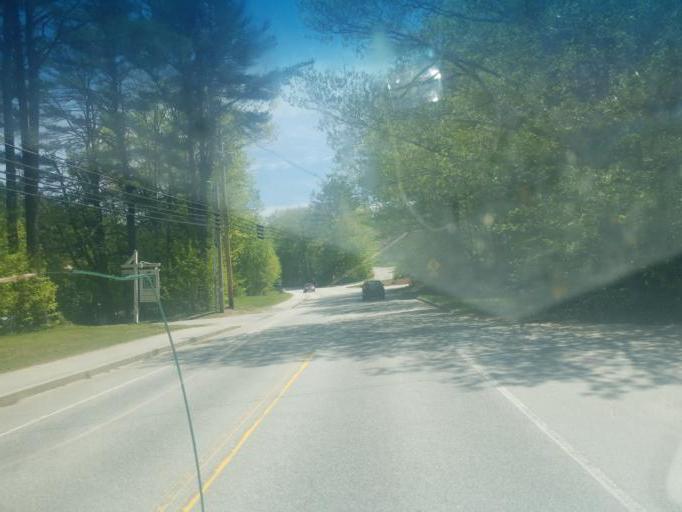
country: US
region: New Hampshire
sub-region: Grafton County
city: Plymouth
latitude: 43.7666
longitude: -71.7156
